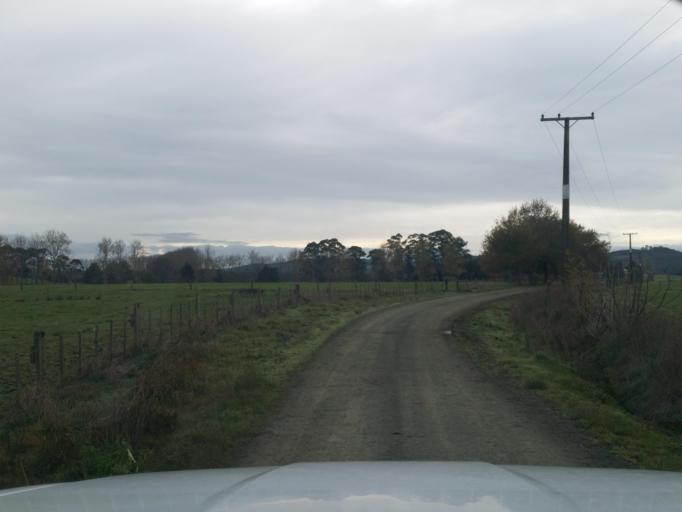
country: NZ
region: Northland
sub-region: Whangarei
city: Maungatapere
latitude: -35.8005
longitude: 174.0514
